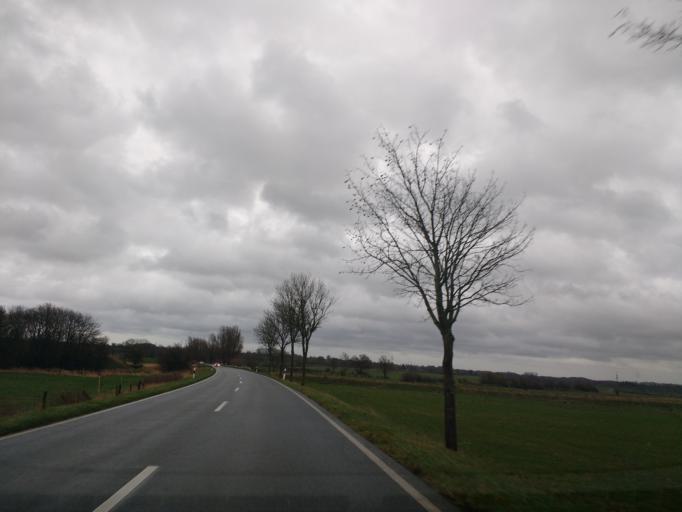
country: DE
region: Schleswig-Holstein
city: Blekendorf
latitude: 54.3027
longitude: 10.6541
